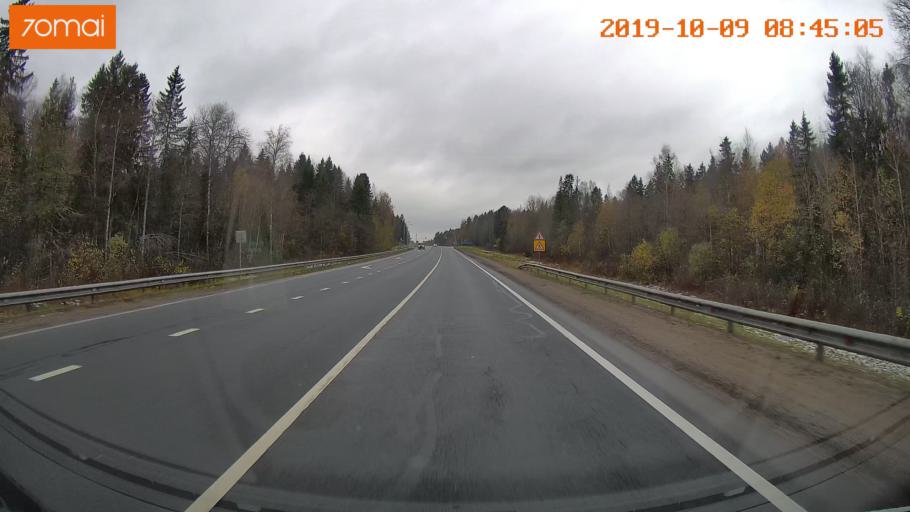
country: RU
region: Vologda
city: Gryazovets
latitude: 59.0445
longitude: 40.0984
